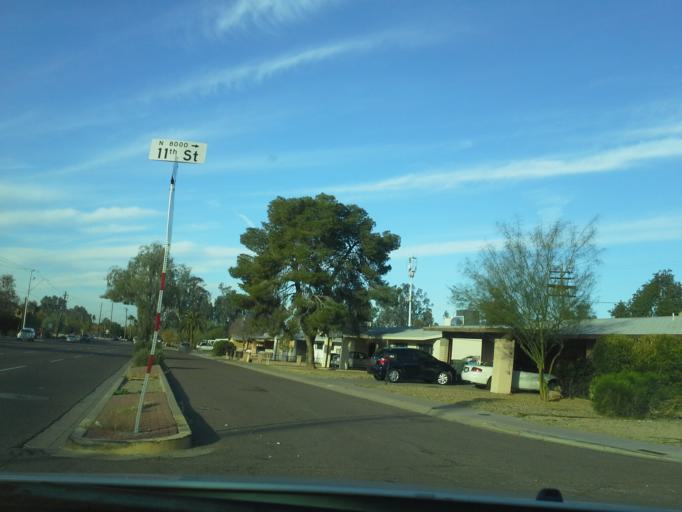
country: US
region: Arizona
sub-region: Maricopa County
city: Phoenix
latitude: 33.5530
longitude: -112.0586
